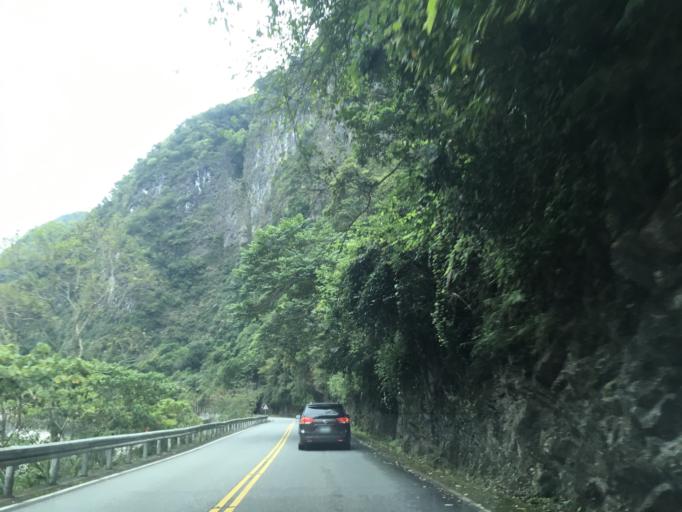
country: TW
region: Taiwan
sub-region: Hualien
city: Hualian
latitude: 24.1693
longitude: 121.6028
